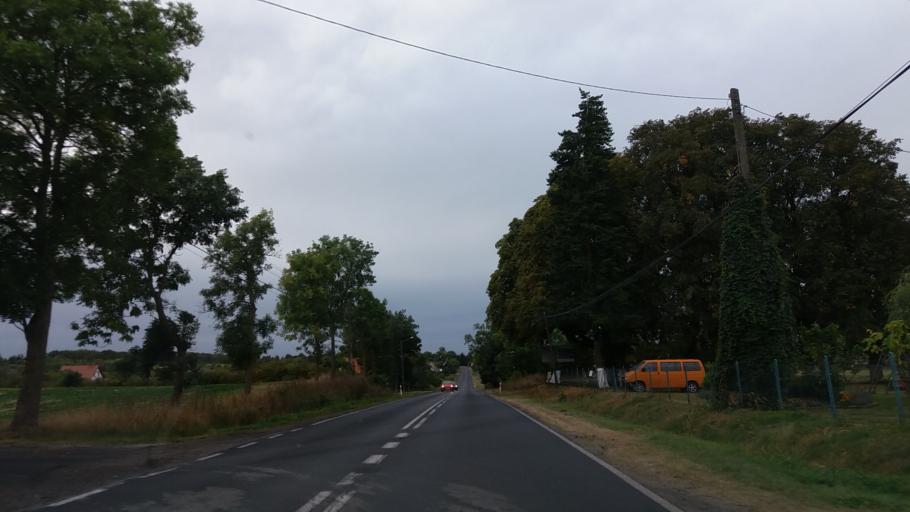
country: PL
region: West Pomeranian Voivodeship
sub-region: Powiat mysliborski
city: Barlinek
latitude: 52.9770
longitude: 15.1896
